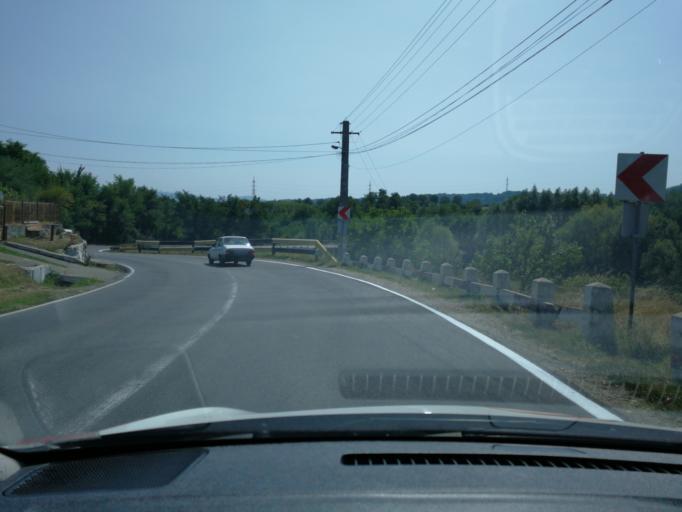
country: RO
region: Prahova
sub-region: Comuna Izvoarele
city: Homoraciu
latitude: 45.2509
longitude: 26.0246
